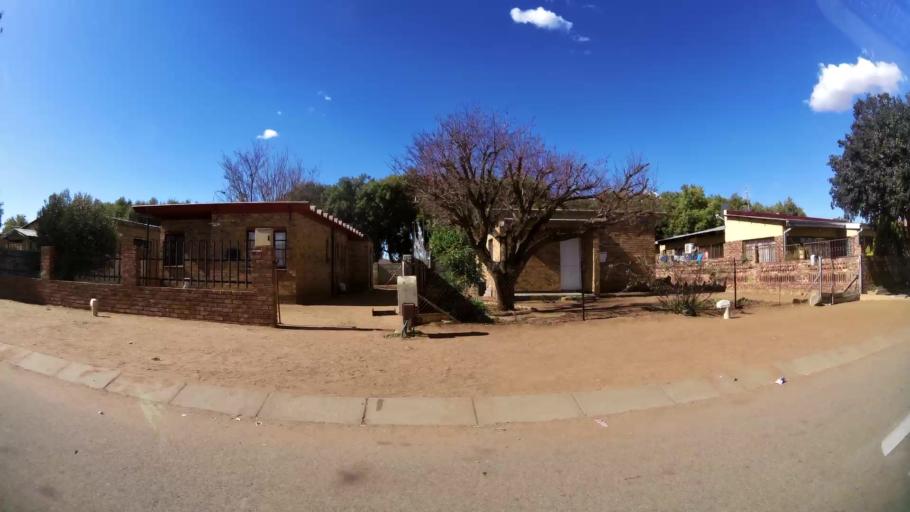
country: ZA
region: North-West
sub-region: Dr Kenneth Kaunda District Municipality
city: Klerksdorp
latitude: -26.8705
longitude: 26.5882
